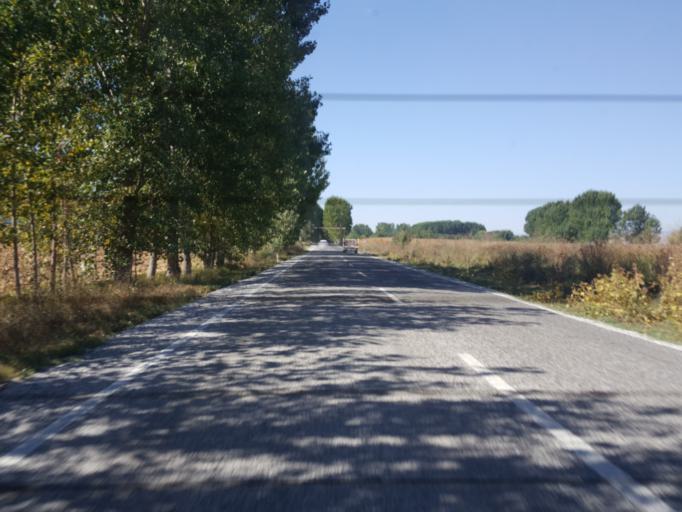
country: TR
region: Tokat
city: Pazar
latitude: 40.2690
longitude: 36.2195
